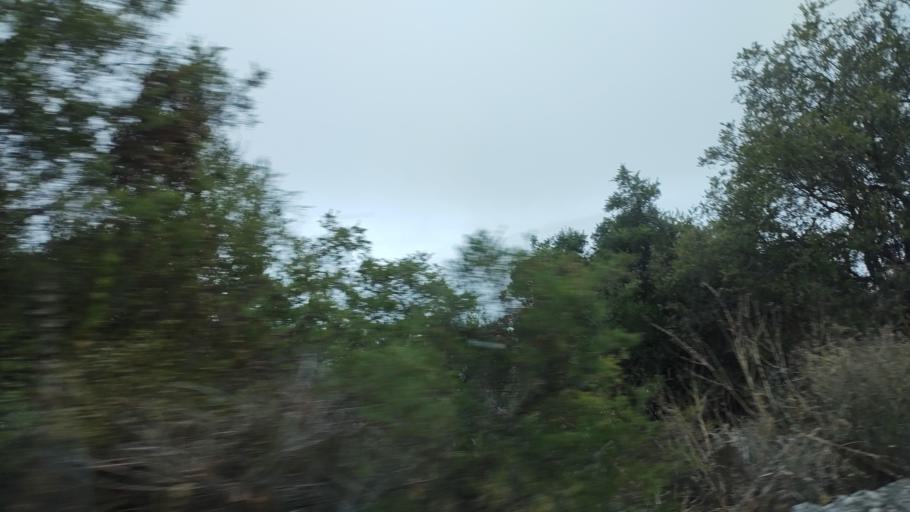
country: GI
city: Gibraltar
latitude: 36.1316
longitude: -5.3479
